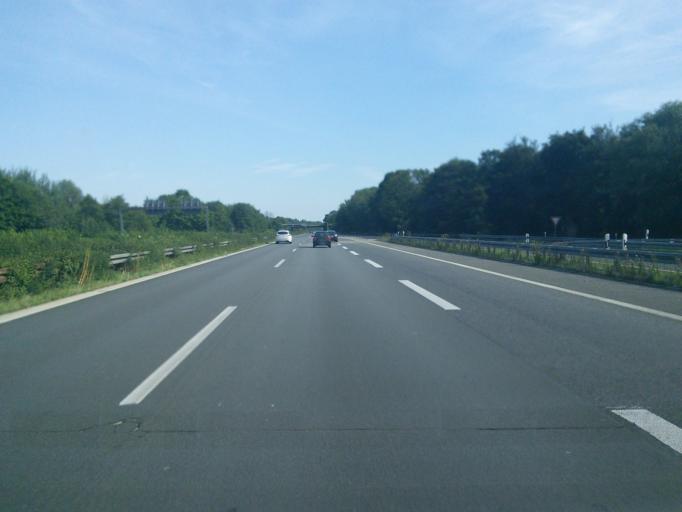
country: DE
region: North Rhine-Westphalia
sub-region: Regierungsbezirk Koln
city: Mengenich
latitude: 50.9921
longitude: 6.8970
